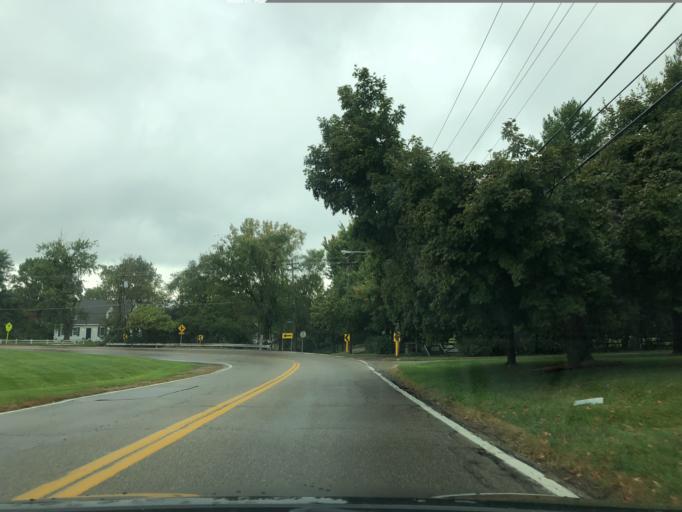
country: US
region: Ohio
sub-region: Hamilton County
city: Finneytown
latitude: 39.2065
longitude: -84.5017
